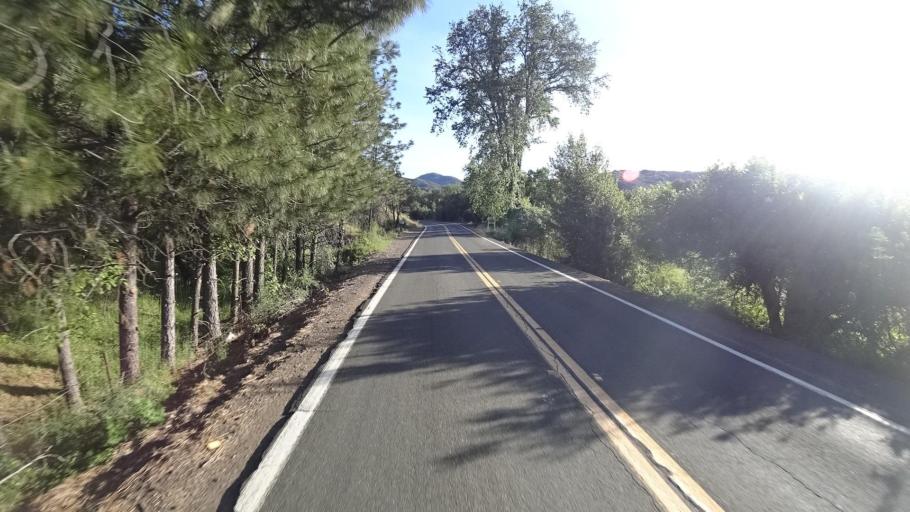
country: US
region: California
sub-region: Lake County
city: North Lakeport
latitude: 39.1195
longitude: -122.9884
